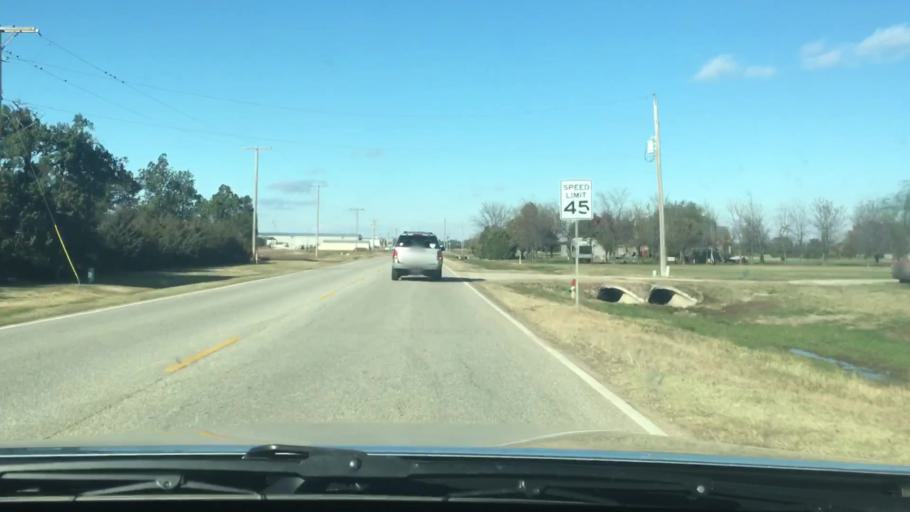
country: US
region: Kansas
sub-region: Sedgwick County
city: Maize
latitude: 37.7763
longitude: -97.4811
